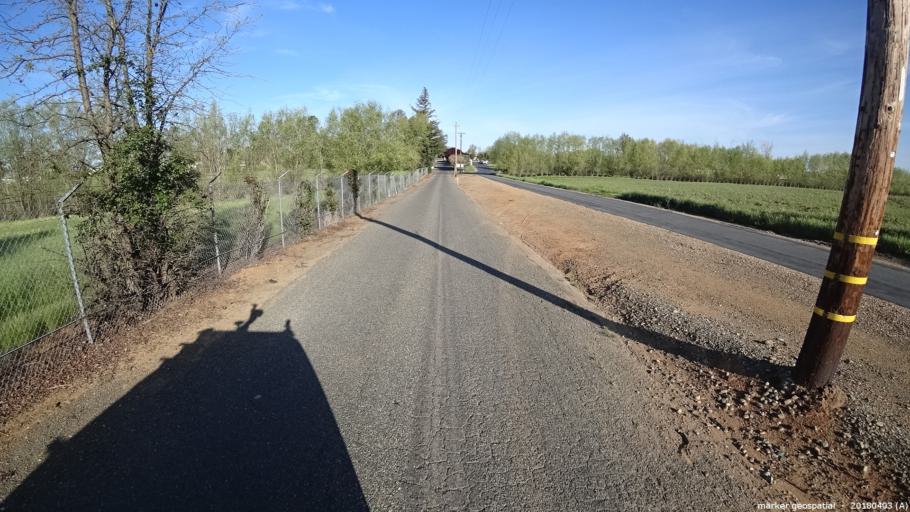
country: US
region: California
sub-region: Sacramento County
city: Wilton
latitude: 38.4463
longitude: -121.1969
